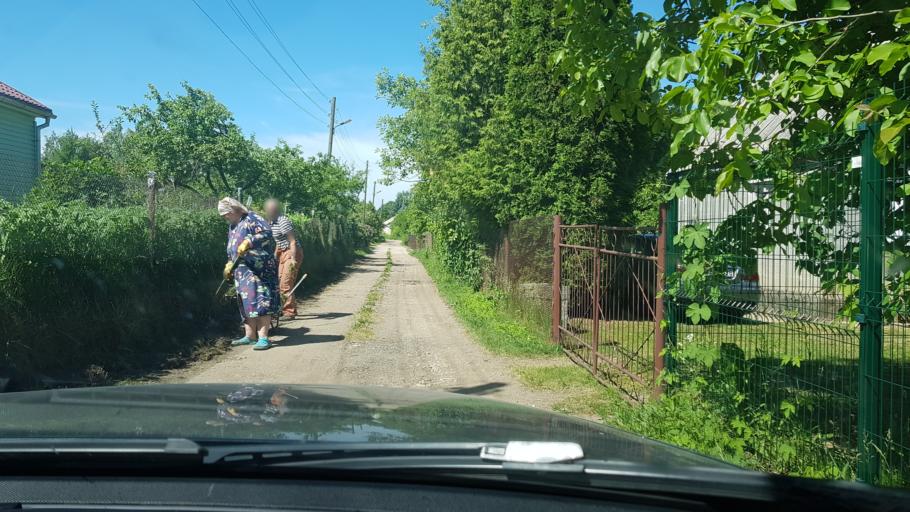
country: LV
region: Daugavpils
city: Daugavpils
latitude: 55.8605
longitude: 26.5727
